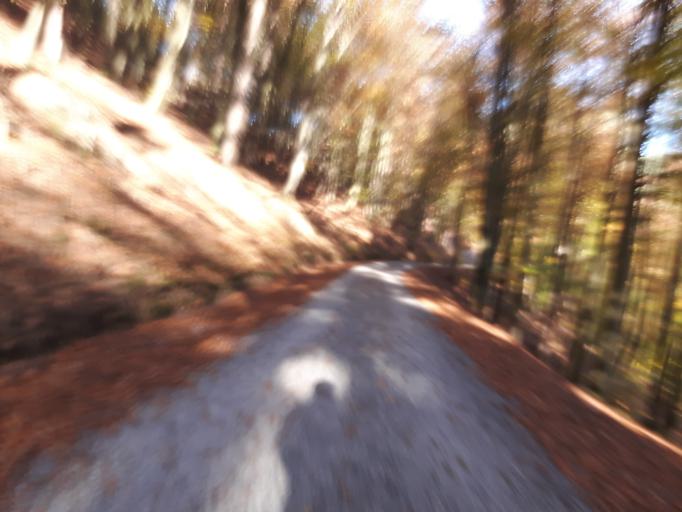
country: DE
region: Bavaria
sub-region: Regierungsbezirk Unterfranken
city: Heimbuchenthal
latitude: 49.8960
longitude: 9.3011
